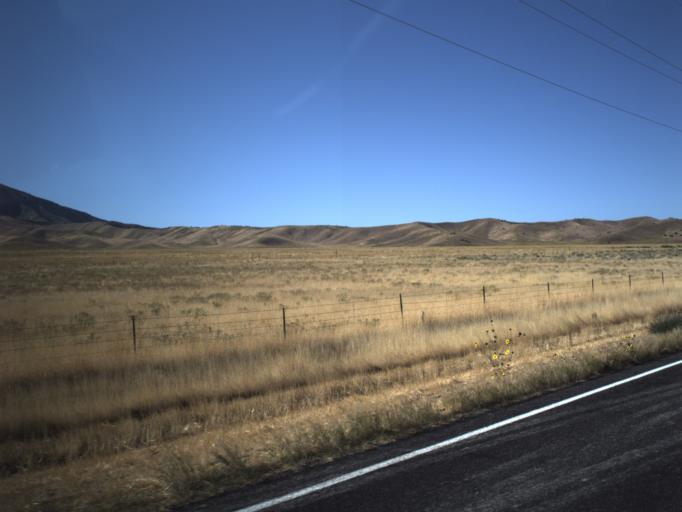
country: US
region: Utah
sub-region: Millard County
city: Delta
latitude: 39.4681
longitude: -112.2761
